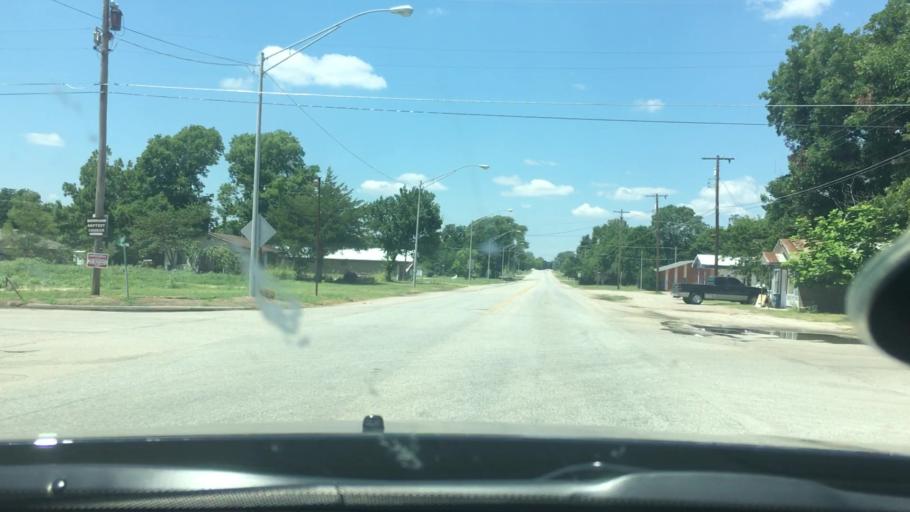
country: US
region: Oklahoma
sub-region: Carter County
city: Dickson
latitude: 34.1863
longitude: -96.8806
